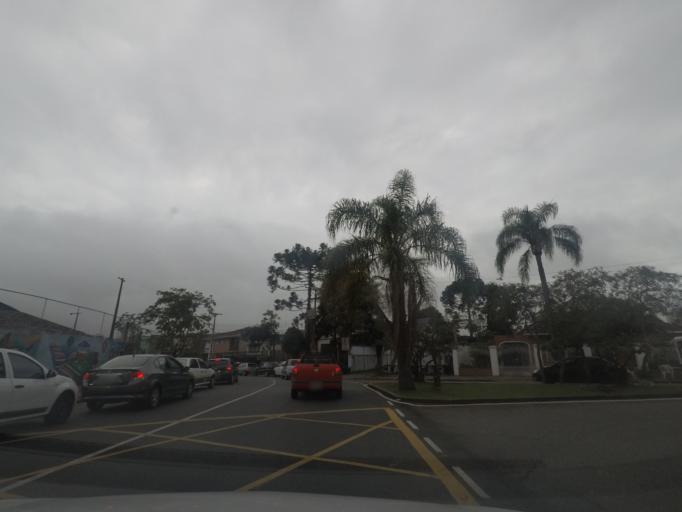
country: BR
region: Parana
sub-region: Curitiba
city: Curitiba
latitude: -25.4413
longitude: -49.2485
